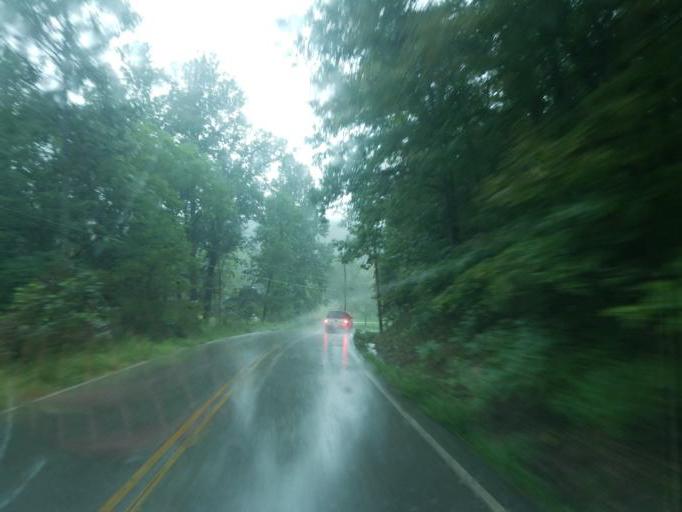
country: US
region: Kentucky
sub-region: Carter County
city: Olive Hill
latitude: 38.3485
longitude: -83.2039
